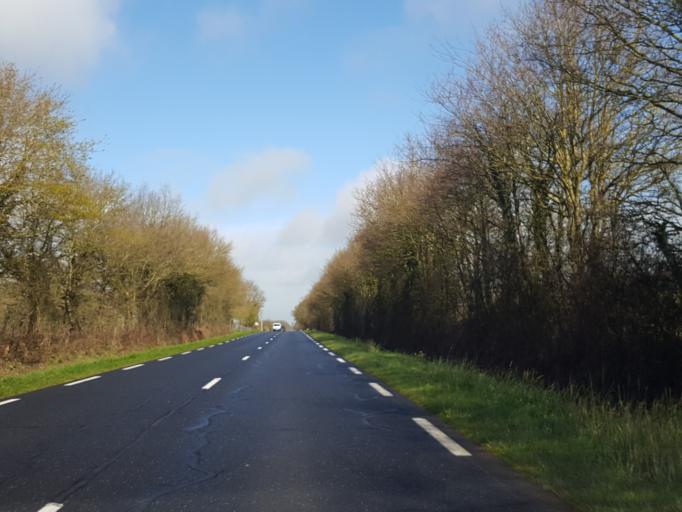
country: FR
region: Pays de la Loire
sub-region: Departement de la Vendee
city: Les Lucs-sur-Boulogne
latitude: 46.8186
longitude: -1.4681
